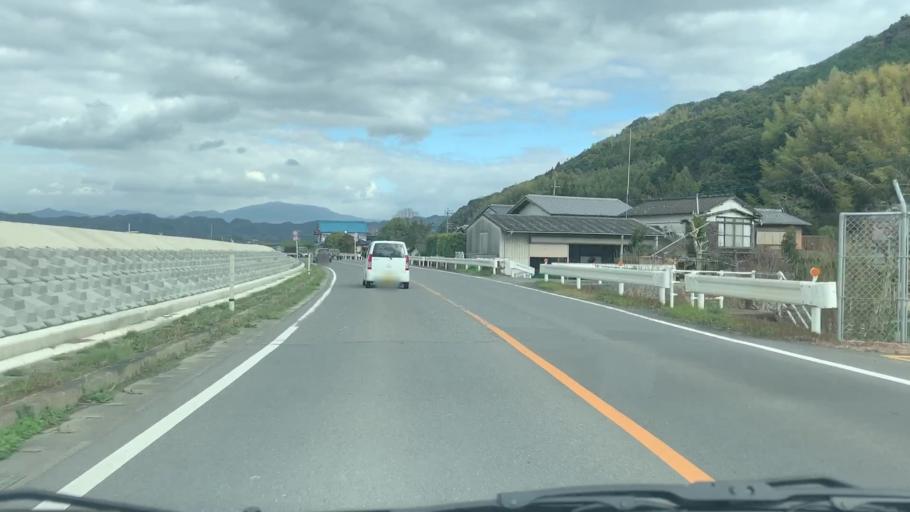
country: JP
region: Saga Prefecture
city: Takeocho-takeo
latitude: 33.2032
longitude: 130.0543
